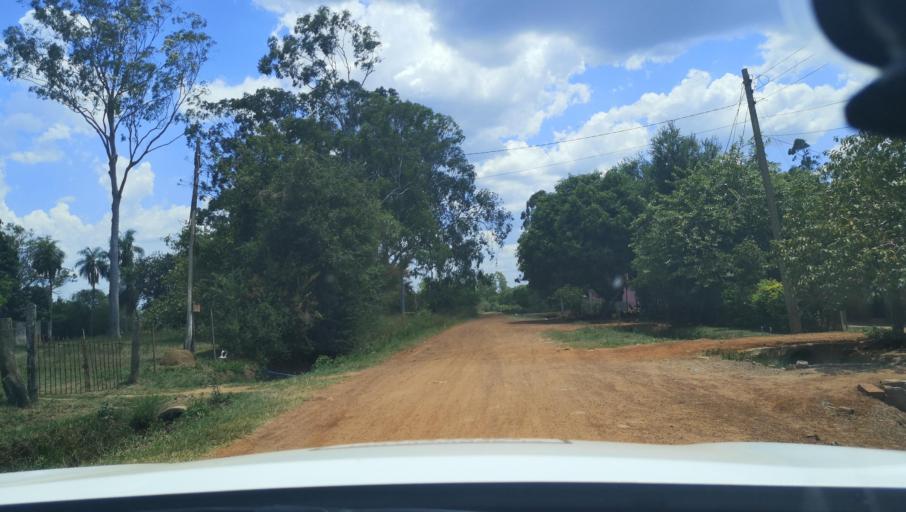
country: PY
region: Itapua
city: Carmen del Parana
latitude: -27.1719
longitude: -56.2382
